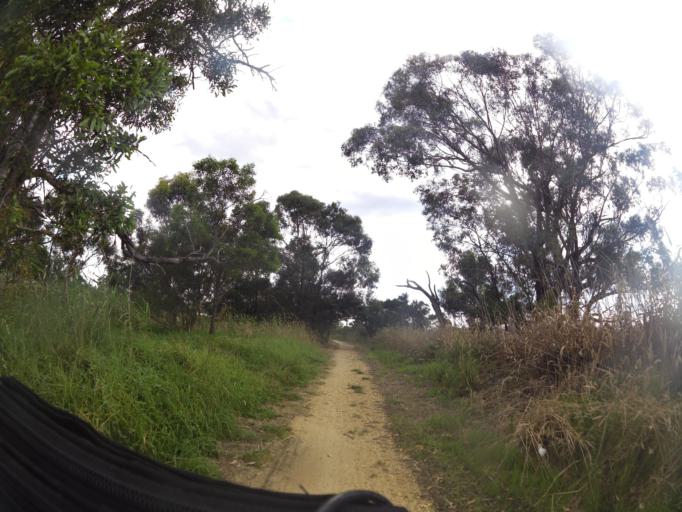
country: AU
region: Victoria
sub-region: Latrobe
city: Traralgon
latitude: -38.0517
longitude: 146.6291
